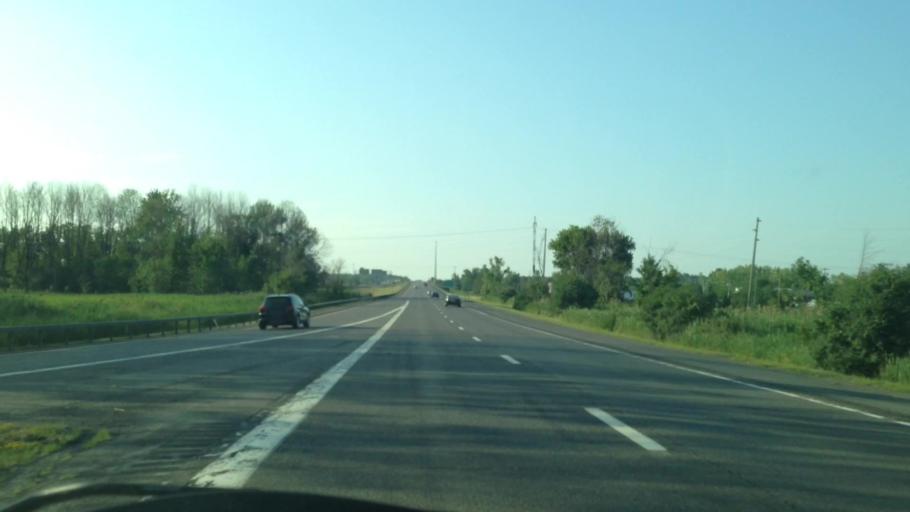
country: US
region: New York
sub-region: Onondaga County
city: East Syracuse
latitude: 43.0571
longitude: -76.0509
